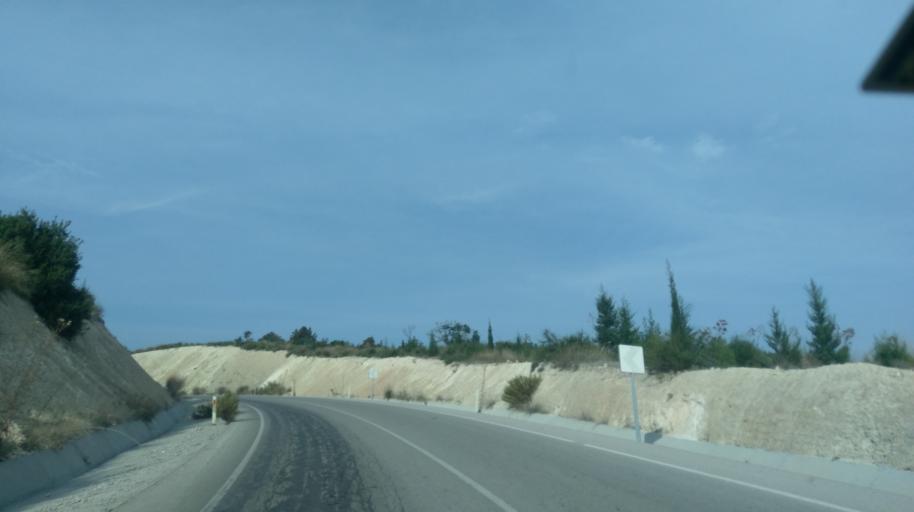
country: CY
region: Ammochostos
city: Trikomo
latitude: 35.4268
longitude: 33.9788
